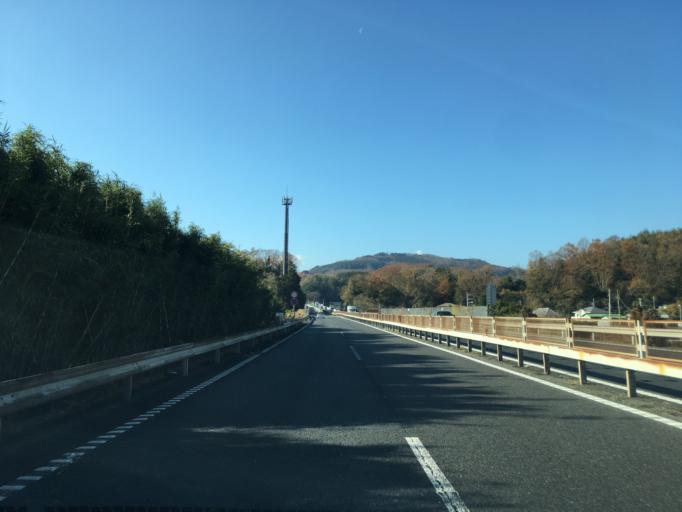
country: JP
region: Kanagawa
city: Ninomiya
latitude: 35.3062
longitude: 139.2282
